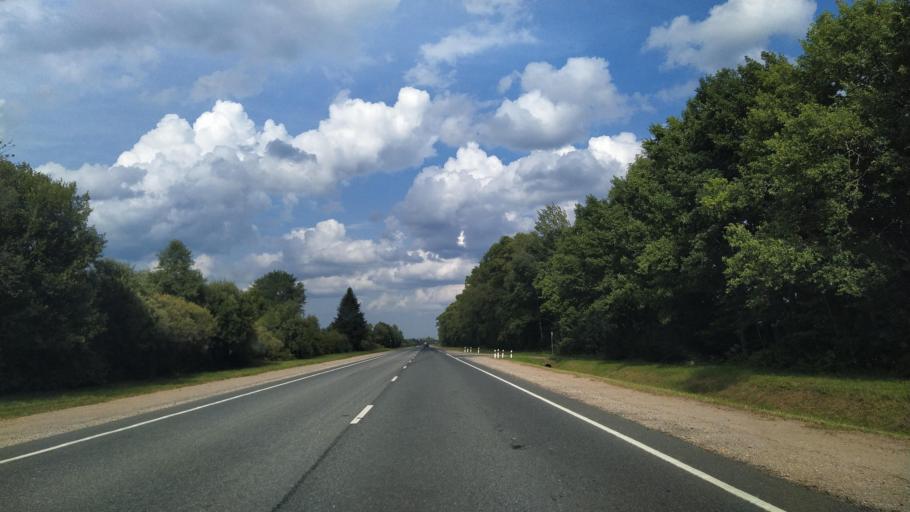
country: RU
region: Novgorod
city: Shimsk
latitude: 58.1915
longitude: 30.5668
